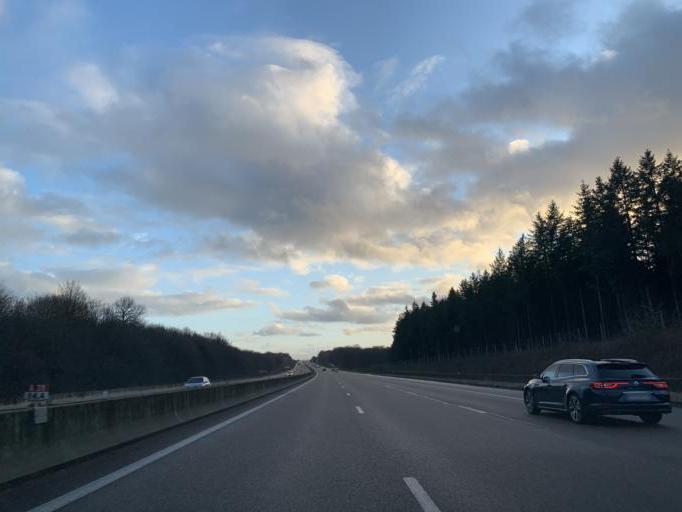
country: FR
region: Bourgogne
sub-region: Departement de la Cote-d'Or
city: Selongey
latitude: 47.6597
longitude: 5.1751
